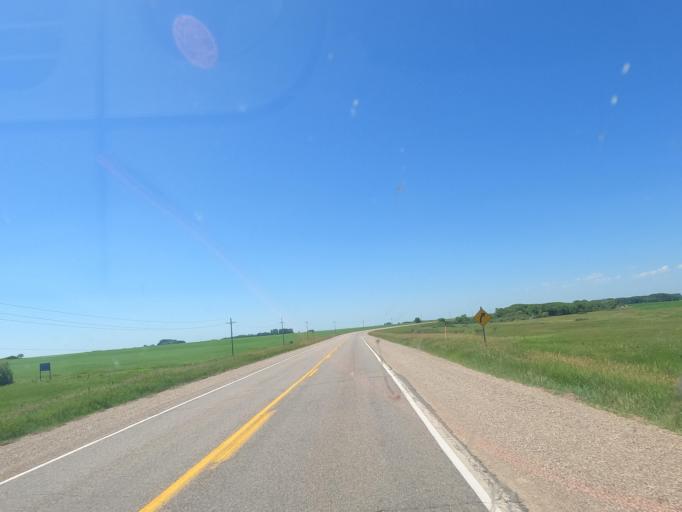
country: CA
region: Manitoba
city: Souris
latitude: 49.6206
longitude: -100.2864
